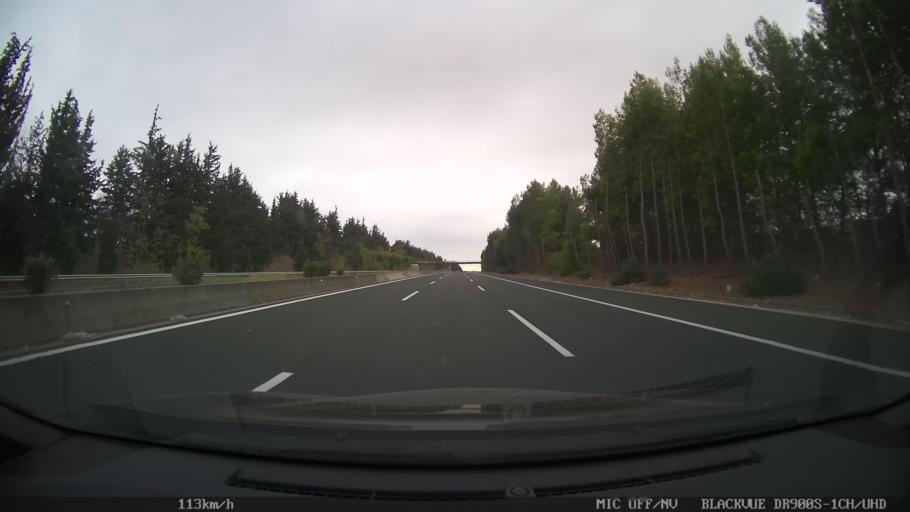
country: GR
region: Central Macedonia
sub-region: Nomos Pierias
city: Kitros
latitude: 40.3829
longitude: 22.6064
